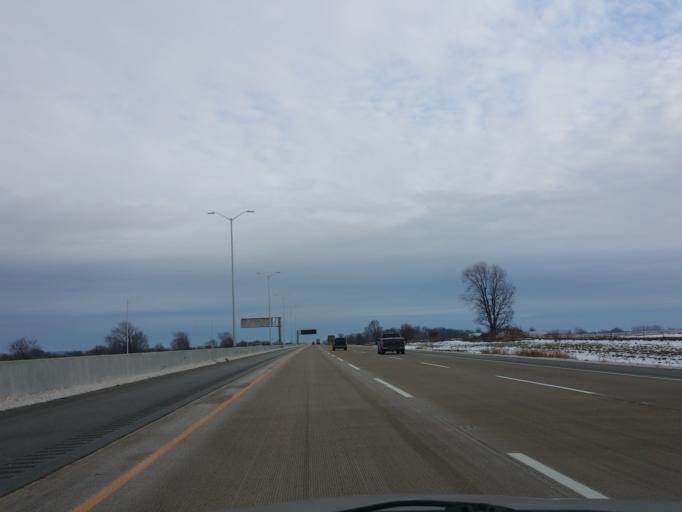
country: US
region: Illinois
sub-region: McHenry County
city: Marengo
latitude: 42.1906
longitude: -88.6552
